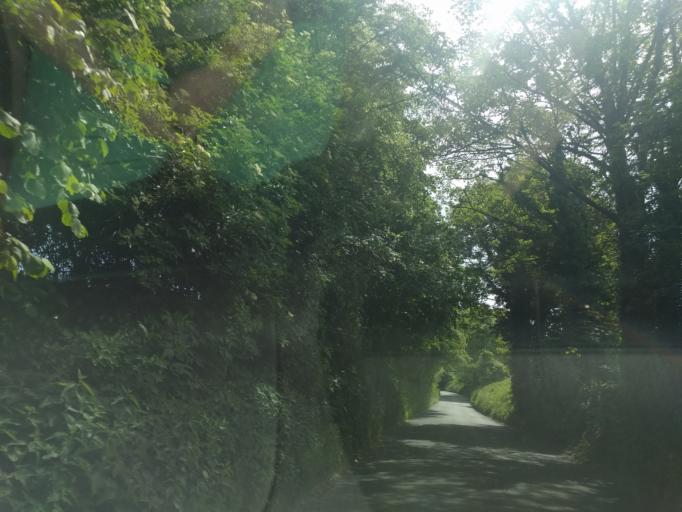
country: GB
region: England
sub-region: Wiltshire
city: Erlestoke
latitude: 51.2812
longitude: -2.0687
